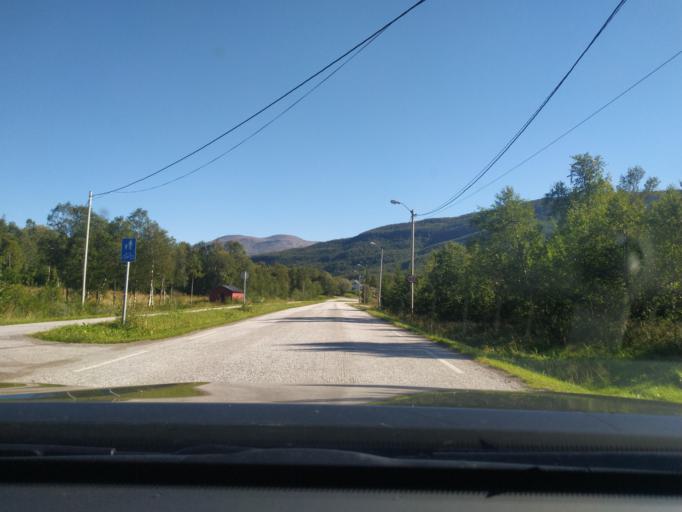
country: NO
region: Troms
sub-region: Salangen
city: Sjovegan
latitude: 68.9381
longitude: 17.7216
